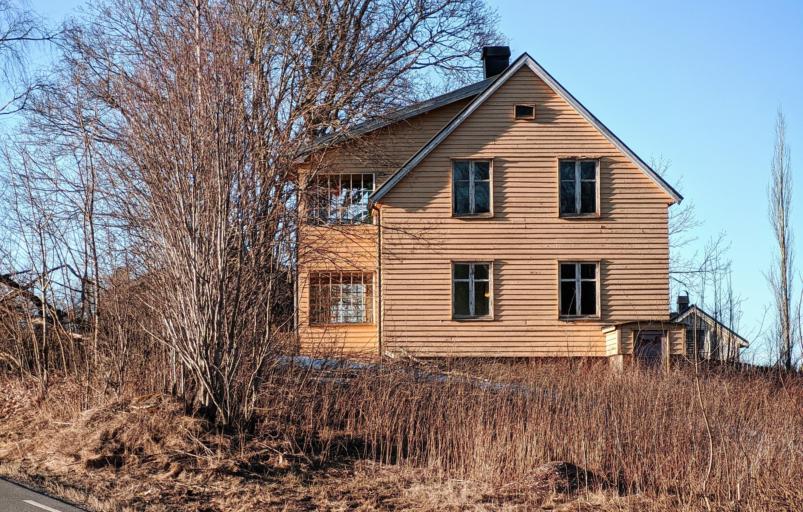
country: NO
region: Akershus
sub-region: Eidsvoll
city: Raholt
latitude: 60.2141
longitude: 11.1400
